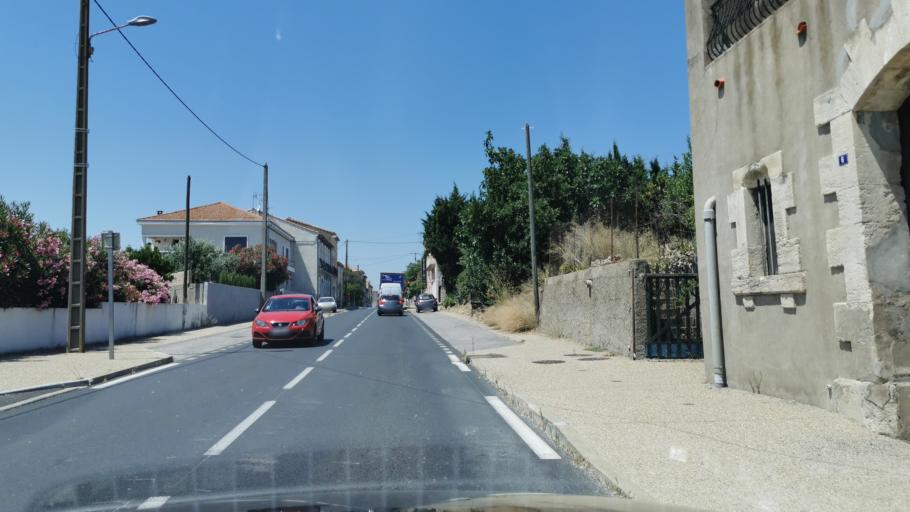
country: FR
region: Languedoc-Roussillon
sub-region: Departement de l'Herault
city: Maureilhan
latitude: 43.3566
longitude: 3.1248
